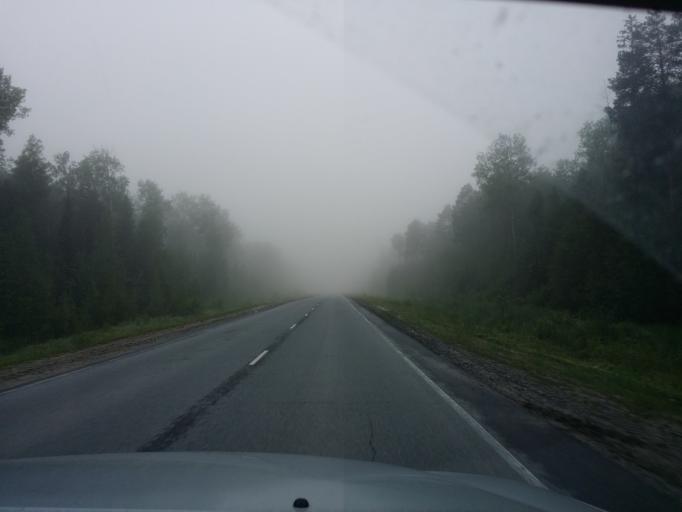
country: RU
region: Khanty-Mansiyskiy Avtonomnyy Okrug
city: Gornopravdinsk
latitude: 59.7064
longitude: 70.1885
